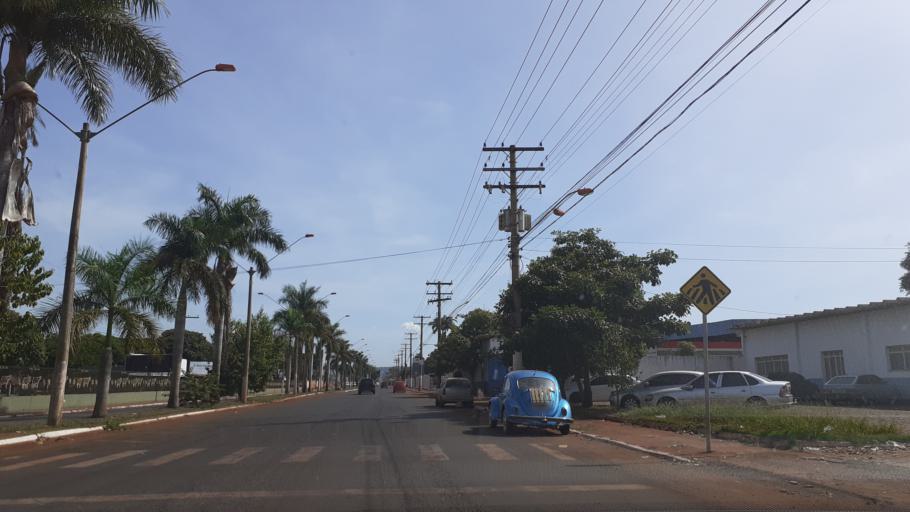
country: BR
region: Goias
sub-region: Itumbiara
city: Itumbiara
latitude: -18.4139
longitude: -49.2399
